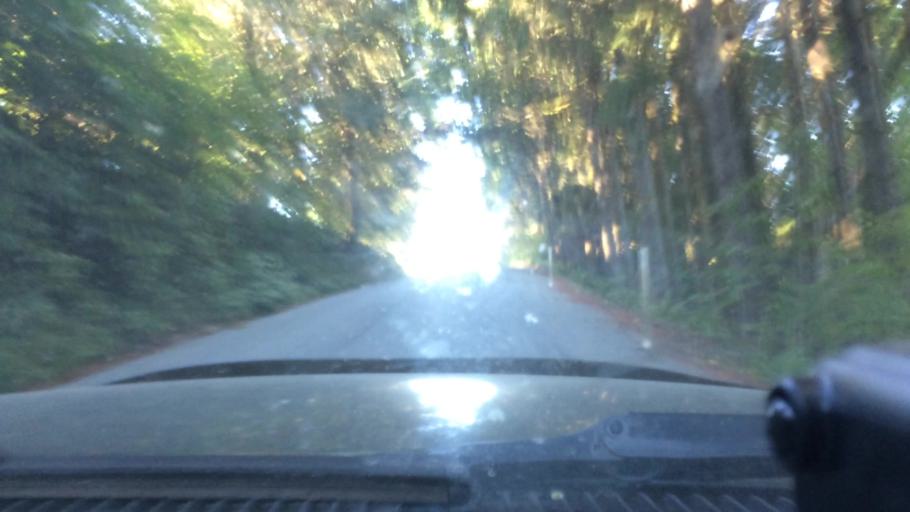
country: US
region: Oregon
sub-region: Yamhill County
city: Newberg
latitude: 45.3723
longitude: -122.9753
